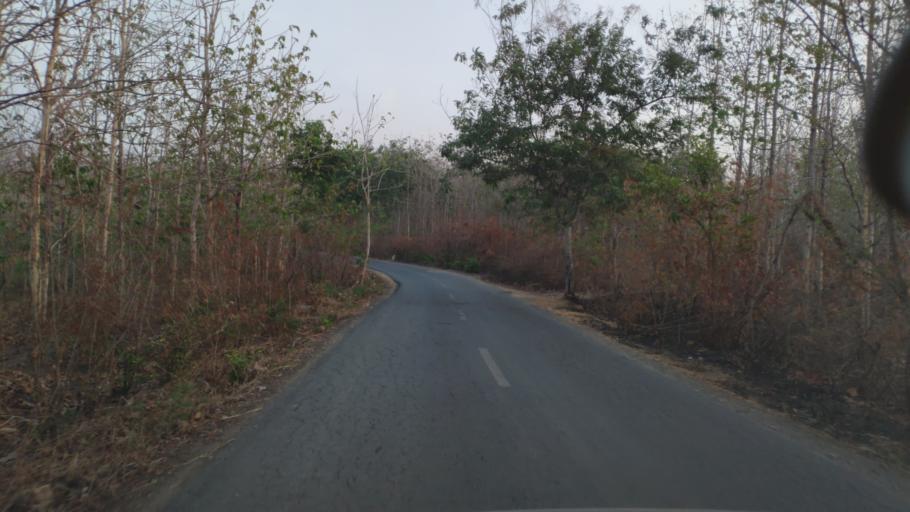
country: ID
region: Central Java
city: Semanggi
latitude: -7.0583
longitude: 111.4136
